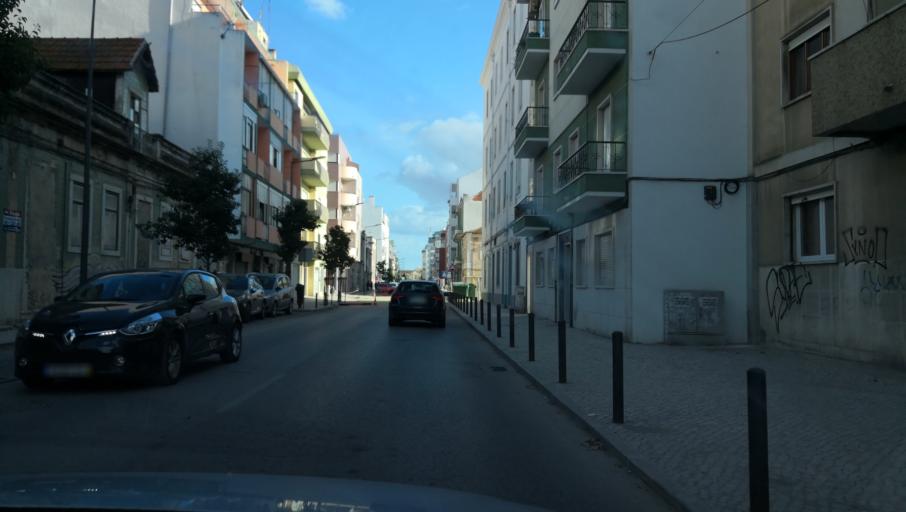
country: PT
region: Setubal
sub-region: Barreiro
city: Barreiro
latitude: 38.6609
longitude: -9.0826
